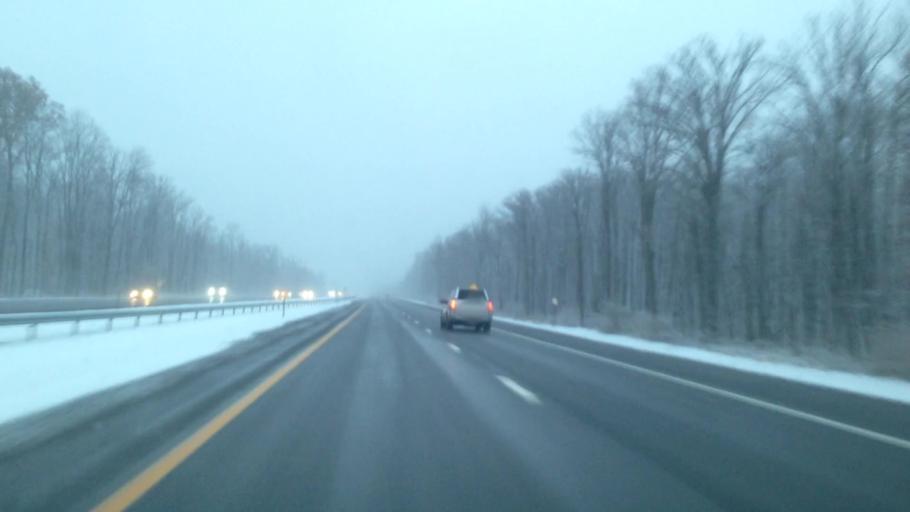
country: US
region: New York
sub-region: Madison County
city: Wampsville
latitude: 43.1037
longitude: -75.7068
